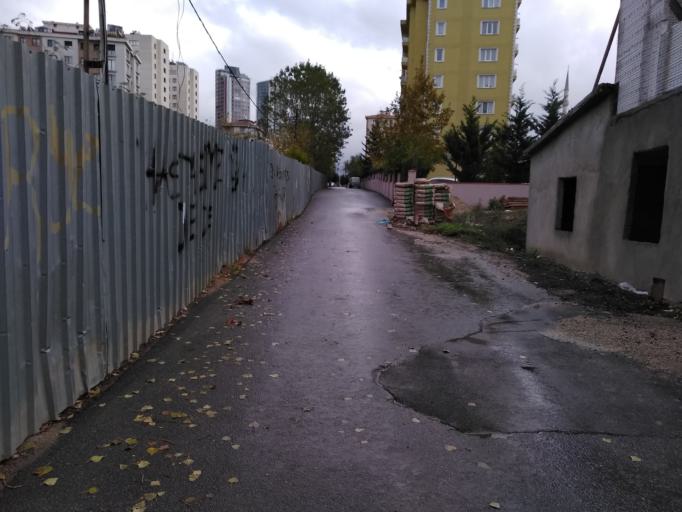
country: TR
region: Istanbul
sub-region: Atasehir
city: Atasehir
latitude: 40.9814
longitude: 29.1247
